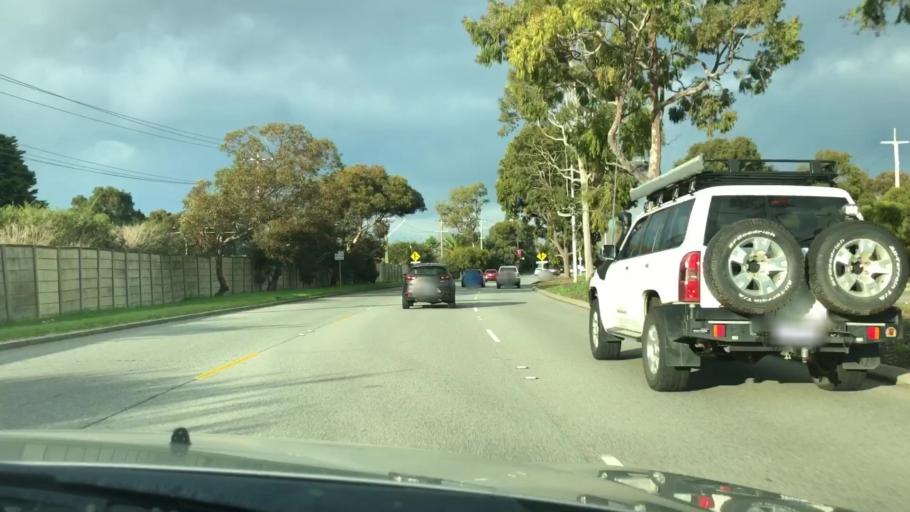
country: AU
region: Western Australia
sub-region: Canning
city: Willetton
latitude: -32.0665
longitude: 115.8830
